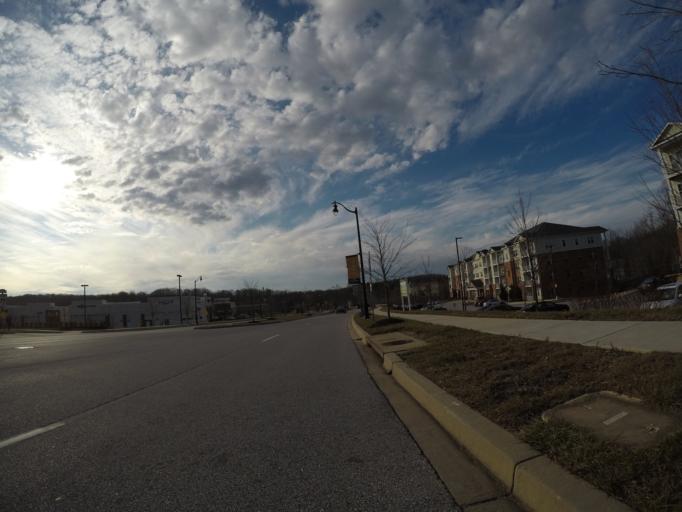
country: US
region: Maryland
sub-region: Howard County
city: Columbia
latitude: 39.2994
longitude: -76.8958
